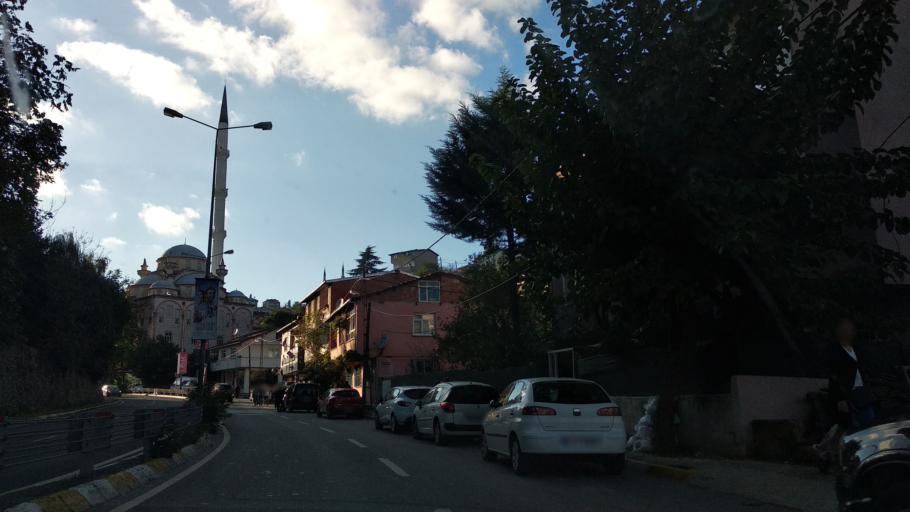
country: TR
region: Istanbul
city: Sisli
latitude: 41.1280
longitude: 29.0362
